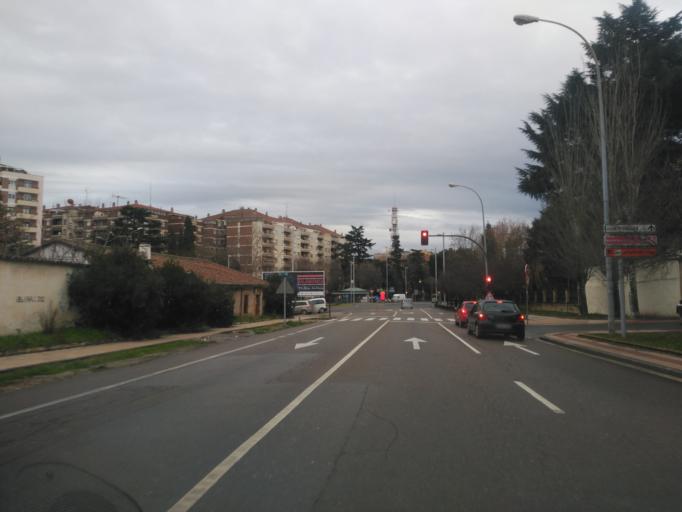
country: ES
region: Castille and Leon
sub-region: Provincia de Salamanca
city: Salamanca
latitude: 40.9768
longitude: -5.6630
